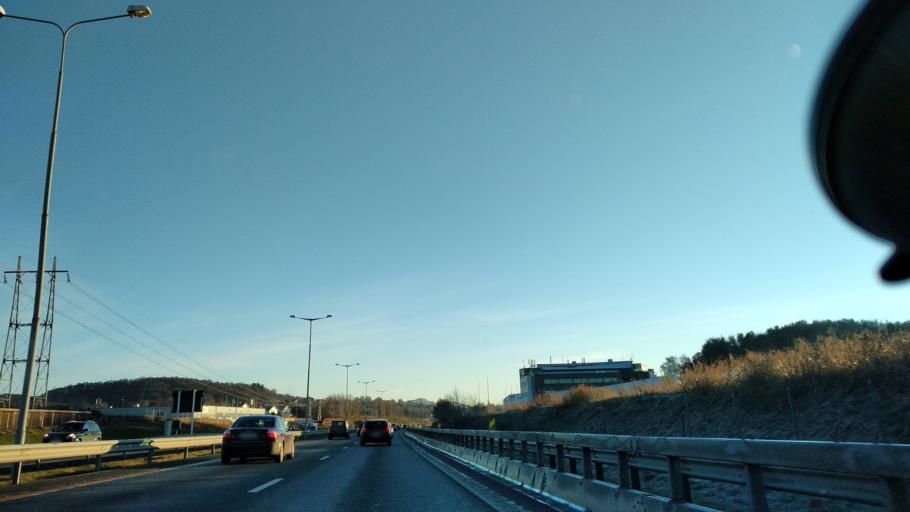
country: NO
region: Rogaland
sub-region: Sola
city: Sola
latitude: 58.9038
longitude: 5.7036
